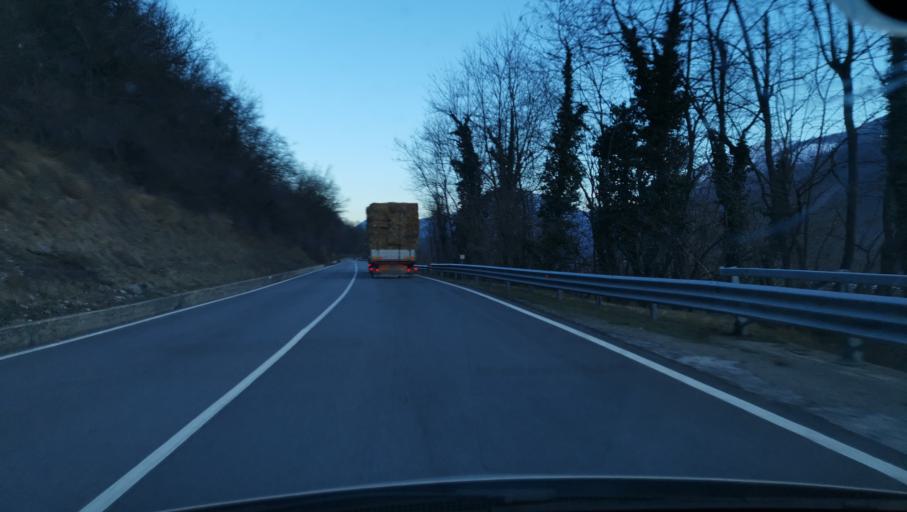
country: IT
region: Piedmont
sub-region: Provincia di Cuneo
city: Demonte
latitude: 44.3139
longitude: 7.2767
